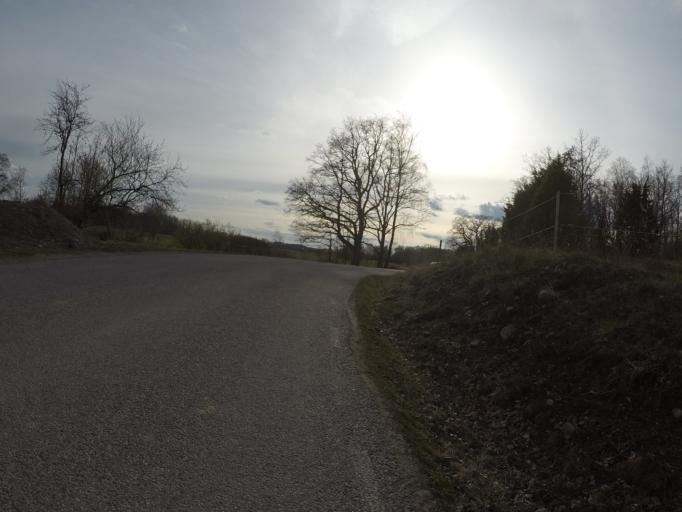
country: SE
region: Soedermanland
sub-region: Eskilstuna Kommun
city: Eskilstuna
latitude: 59.4314
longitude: 16.5459
